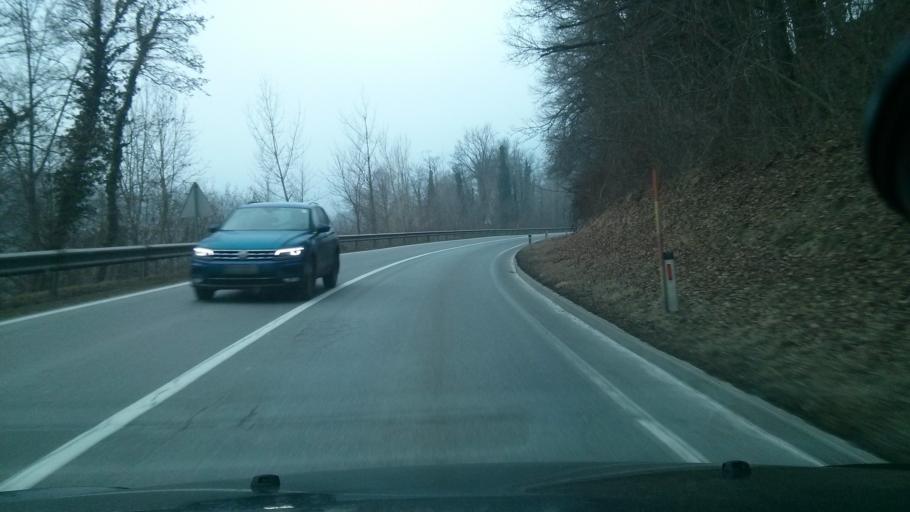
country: SI
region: Litija
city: Litija
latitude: 46.0946
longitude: 14.8032
